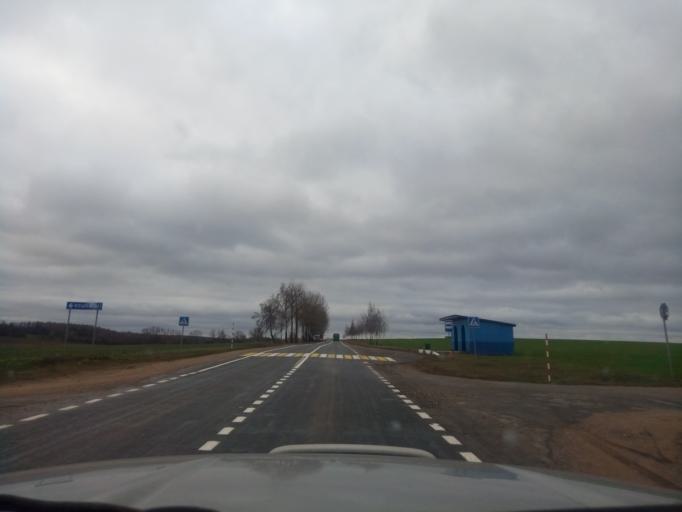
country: BY
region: Minsk
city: Kapyl'
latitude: 53.1827
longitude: 27.1761
